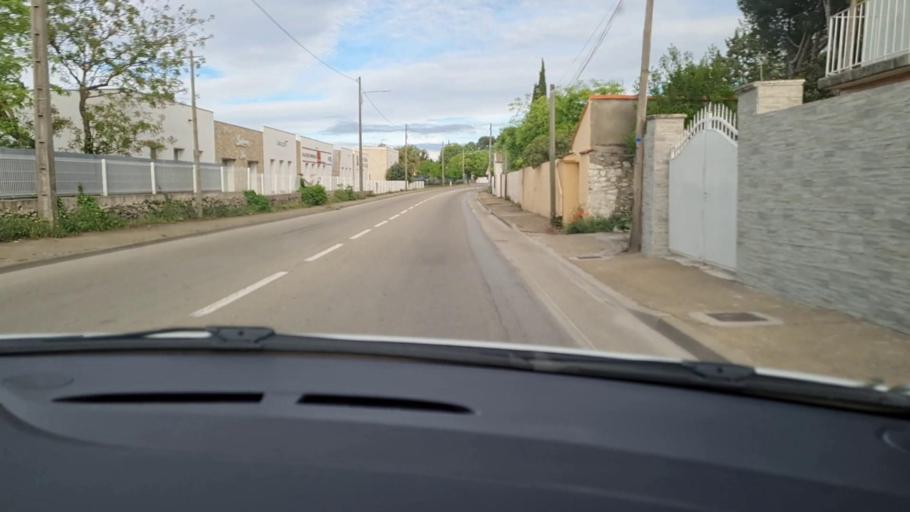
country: FR
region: Languedoc-Roussillon
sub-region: Departement du Gard
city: Nimes
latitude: 43.8414
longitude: 4.3156
